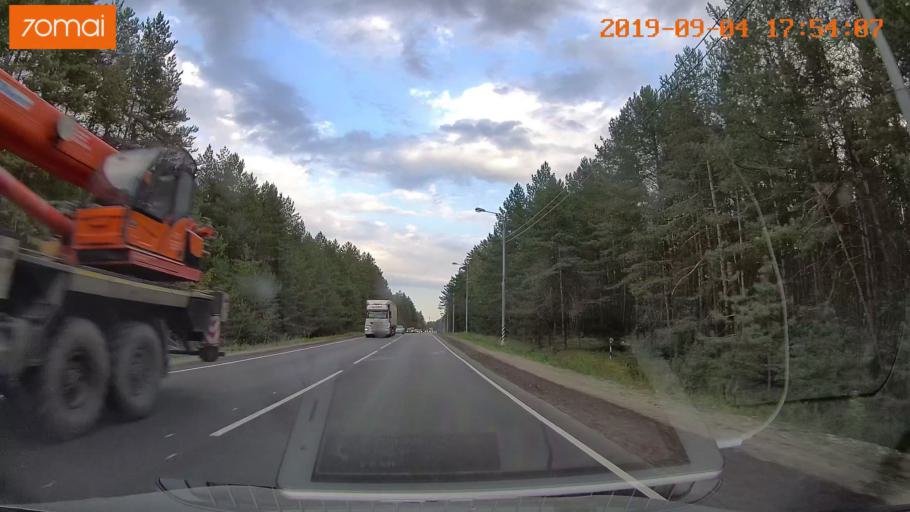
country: RU
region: Moskovskaya
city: Imeni Tsyurupy
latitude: 55.5124
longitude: 38.7366
